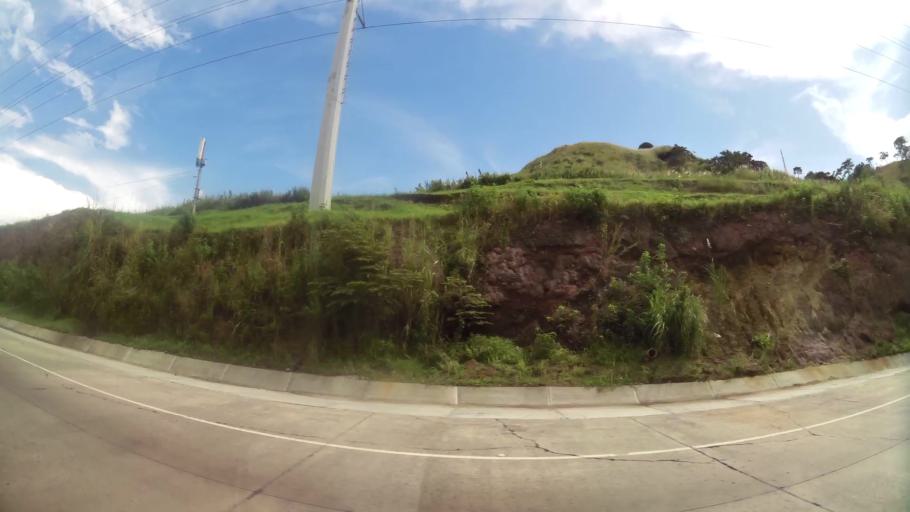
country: PA
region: Panama
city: Las Cumbres
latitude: 9.0538
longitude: -79.5185
